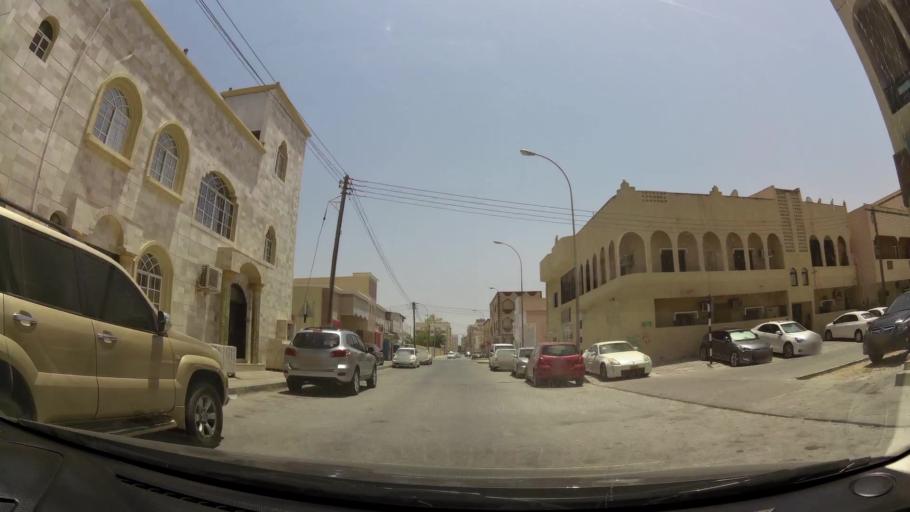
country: OM
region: Zufar
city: Salalah
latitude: 17.0200
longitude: 54.0824
